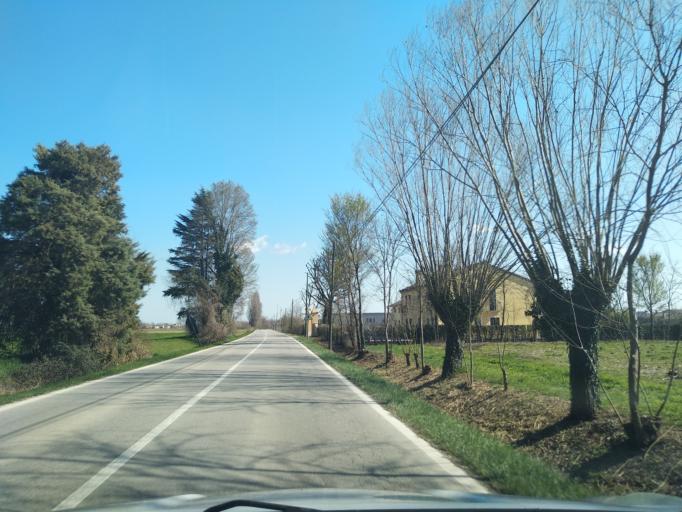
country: IT
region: Veneto
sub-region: Provincia di Padova
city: Taggi
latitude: 45.4653
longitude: 11.8011
